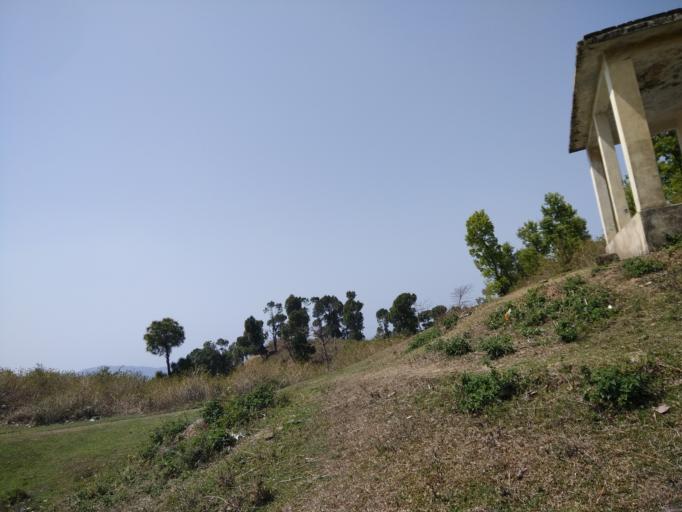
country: IN
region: Himachal Pradesh
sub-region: Kangra
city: Palampur
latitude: 32.0790
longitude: 76.6215
